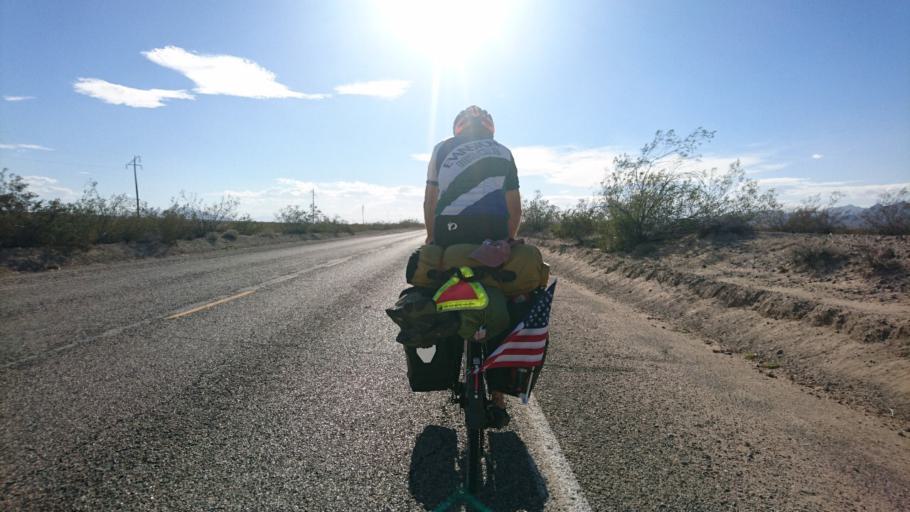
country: US
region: California
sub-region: San Bernardino County
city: Needles
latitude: 34.7171
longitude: -115.2745
